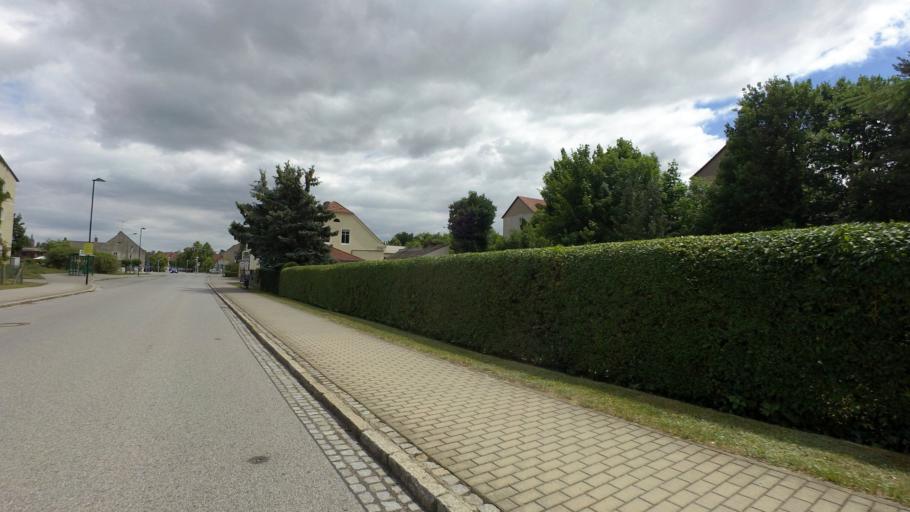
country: DE
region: Brandenburg
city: Luckau
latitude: 51.8509
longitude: 13.7010
